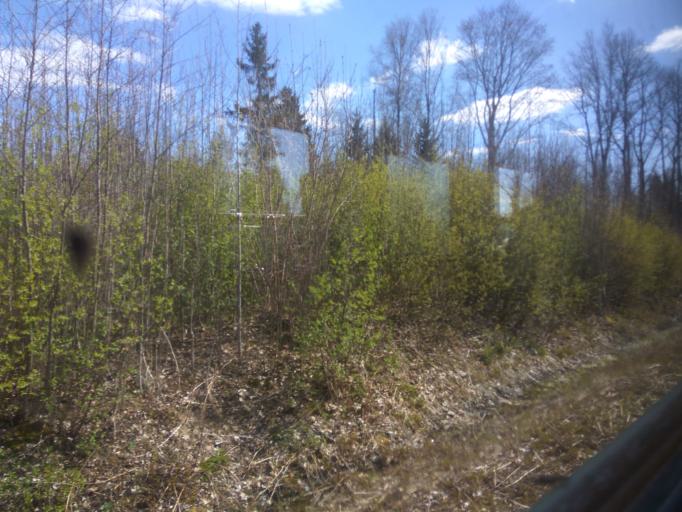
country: LV
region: Aluksnes Rajons
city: Aluksne
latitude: 57.3599
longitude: 27.0316
